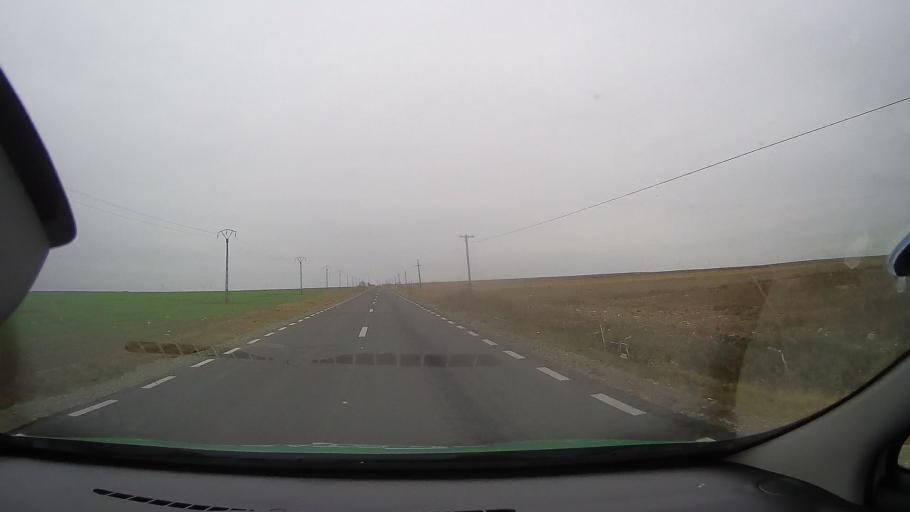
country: RO
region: Constanta
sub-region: Comuna Tortoman
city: Tortoman
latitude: 44.3512
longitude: 28.2164
